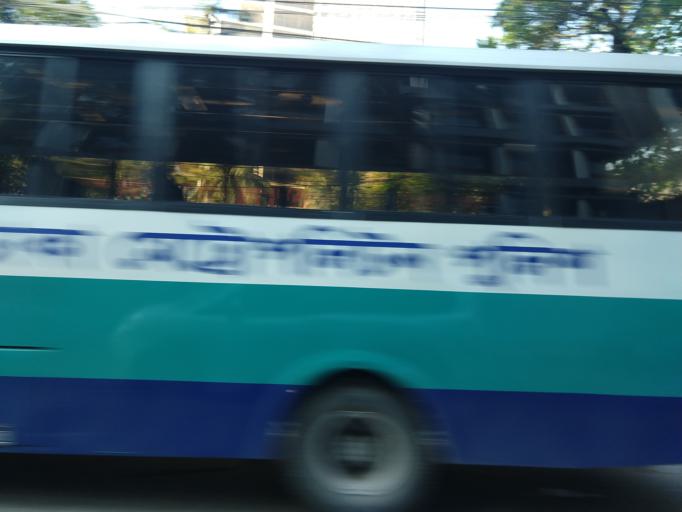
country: BD
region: Dhaka
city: Paltan
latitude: 23.7944
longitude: 90.4122
